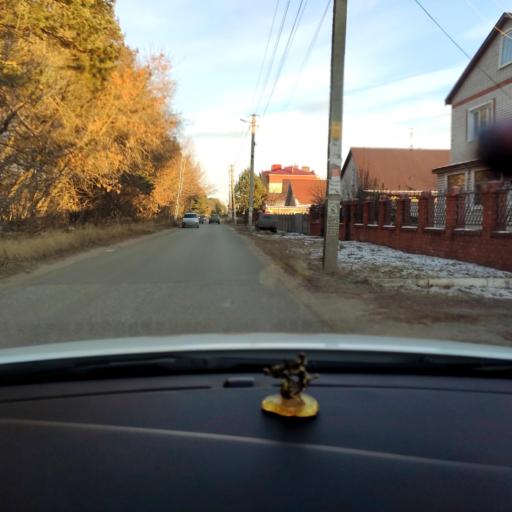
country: RU
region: Tatarstan
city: Stolbishchi
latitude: 55.6126
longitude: 49.1336
